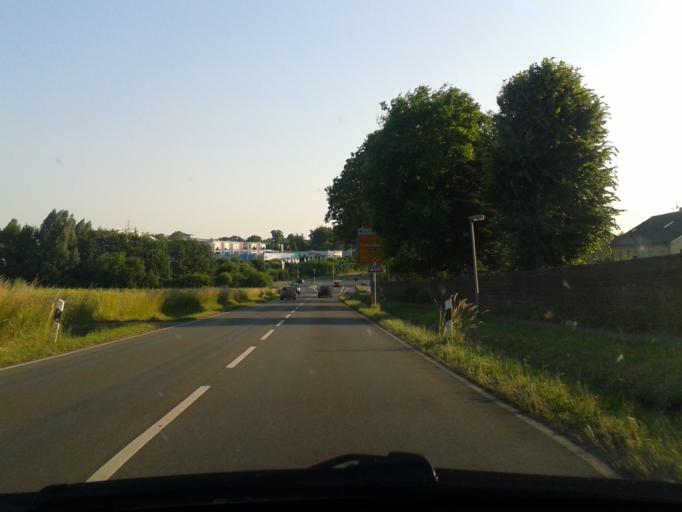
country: DE
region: North Rhine-Westphalia
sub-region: Regierungsbezirk Detmold
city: Detmold
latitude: 51.9492
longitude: 8.9018
